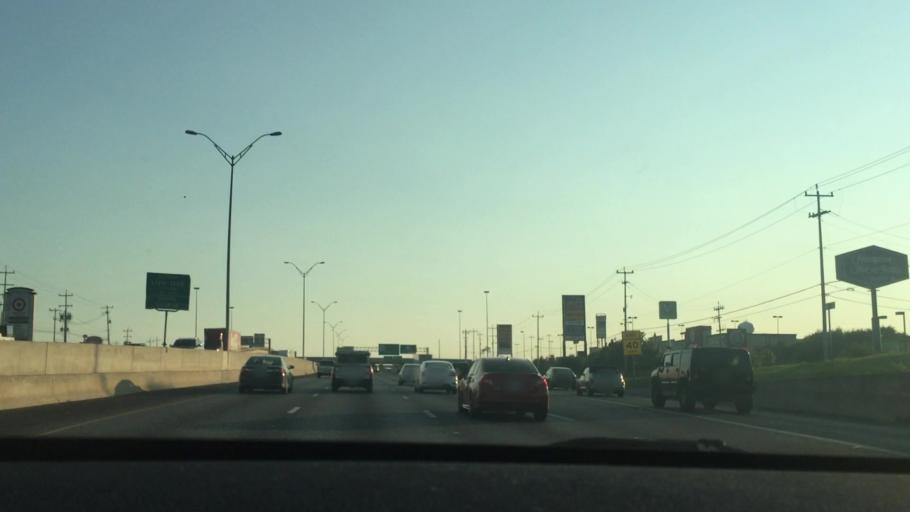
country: US
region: Texas
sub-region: Bexar County
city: Live Oak
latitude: 29.5721
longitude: -98.3285
